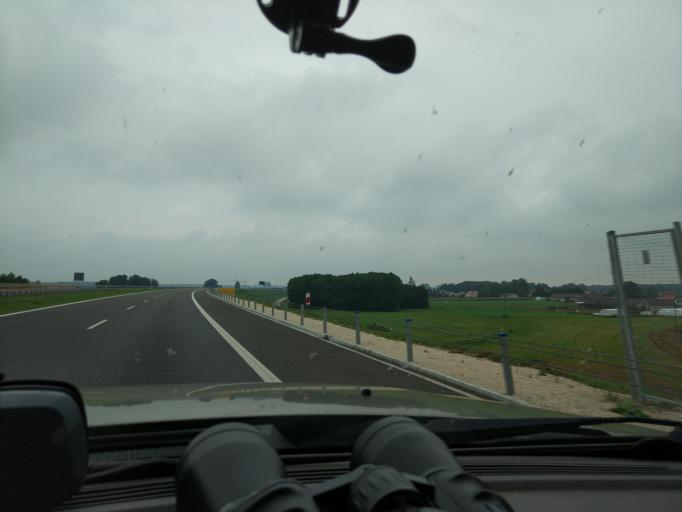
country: PL
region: Podlasie
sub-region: Powiat zambrowski
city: Szumowo
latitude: 52.9425
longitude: 22.1506
